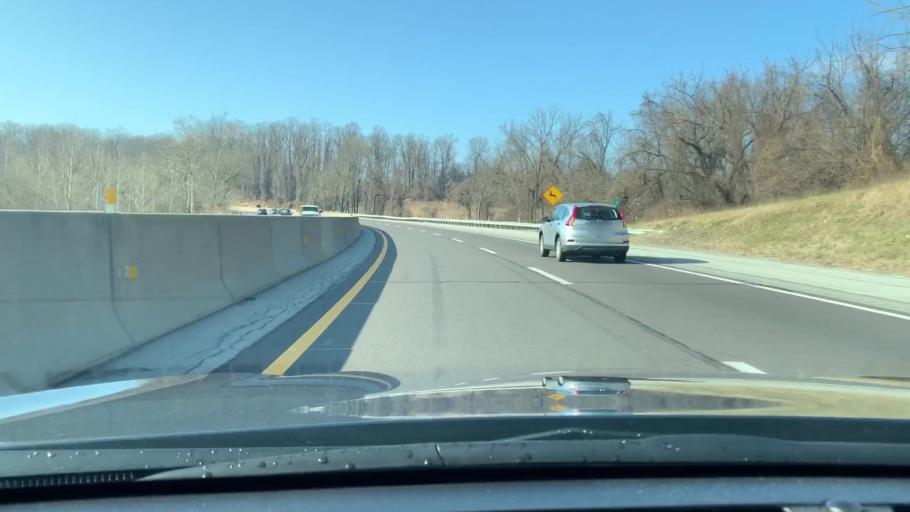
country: US
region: Pennsylvania
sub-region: Chester County
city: Malvern
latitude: 40.0777
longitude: -75.5448
